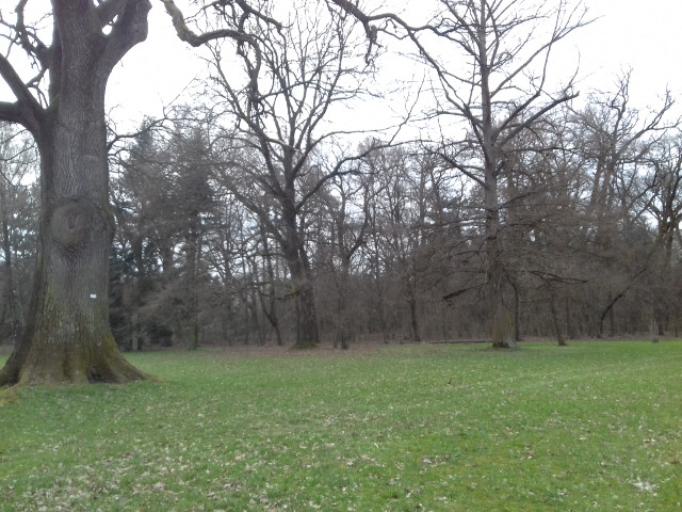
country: HU
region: Bacs-Kiskun
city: Tiszakecske
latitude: 46.8904
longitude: 20.1197
